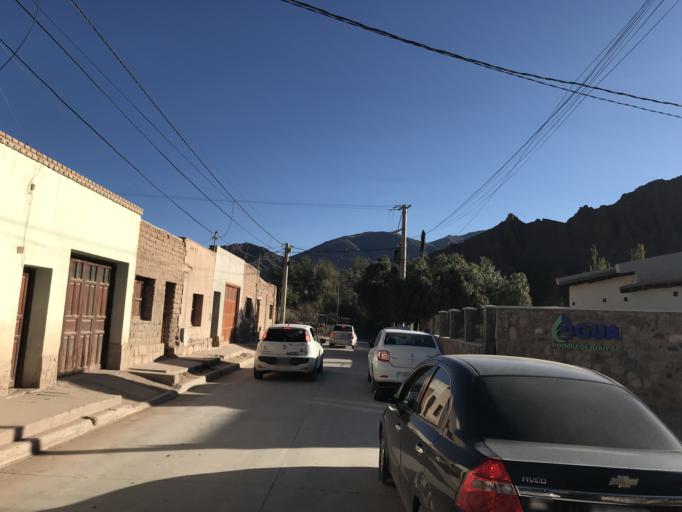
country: AR
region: Jujuy
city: Maimara
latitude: -23.5778
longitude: -65.4008
